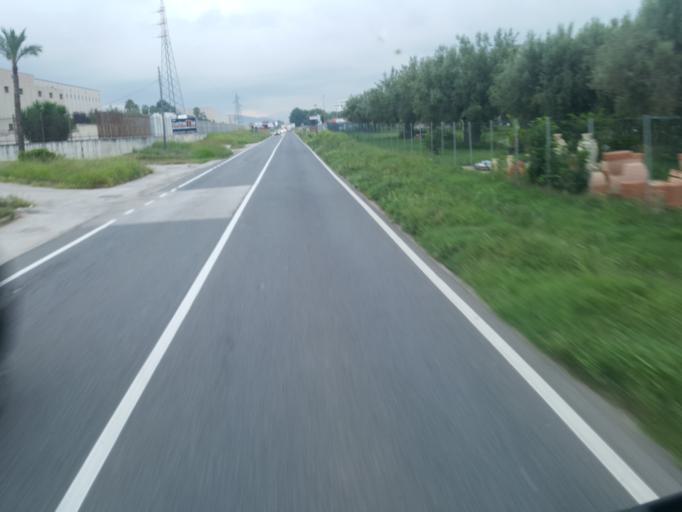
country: IT
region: Campania
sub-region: Provincia di Caserta
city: Pignataro Maggiore
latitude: 41.1663
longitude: 14.1575
